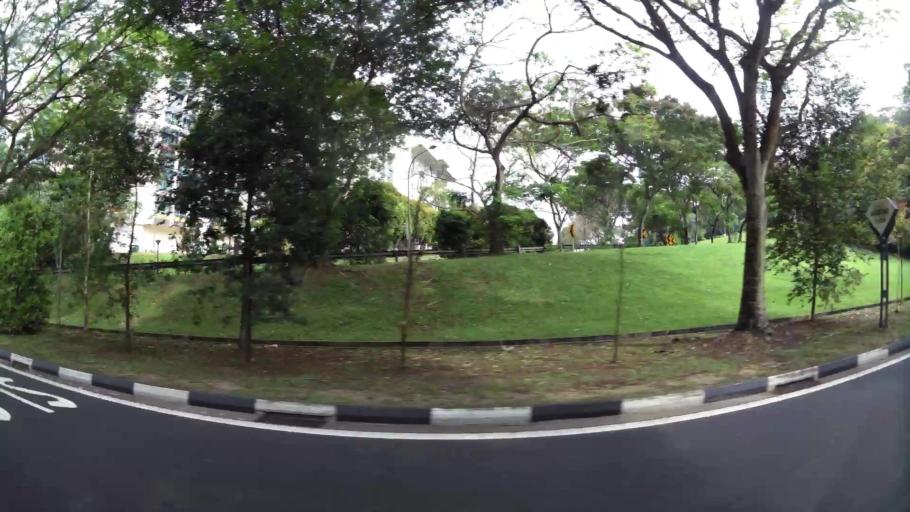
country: MY
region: Johor
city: Johor Bahru
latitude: 1.4269
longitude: 103.7865
